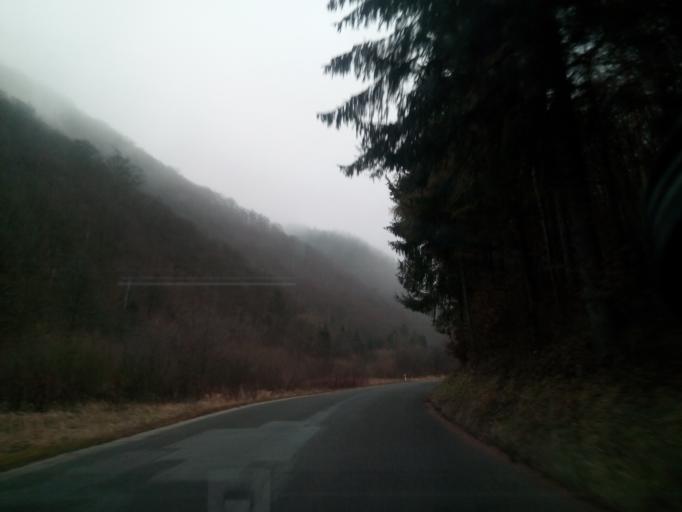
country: SK
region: Kosicky
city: Krompachy
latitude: 48.9426
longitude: 20.9461
